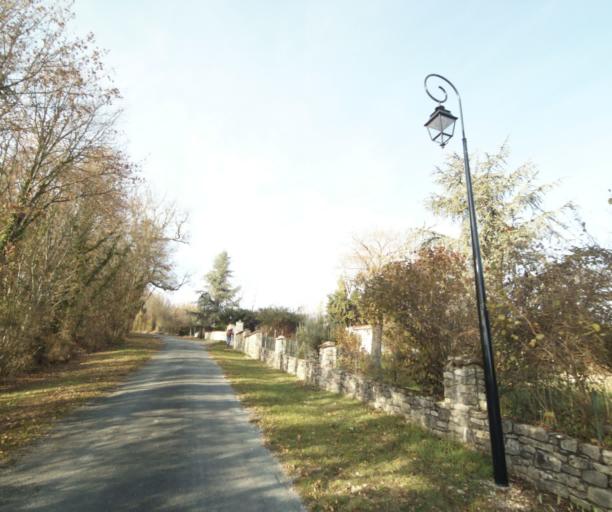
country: FR
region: Poitou-Charentes
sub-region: Departement de la Charente-Maritime
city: Chaniers
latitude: 45.7359
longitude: -0.5107
